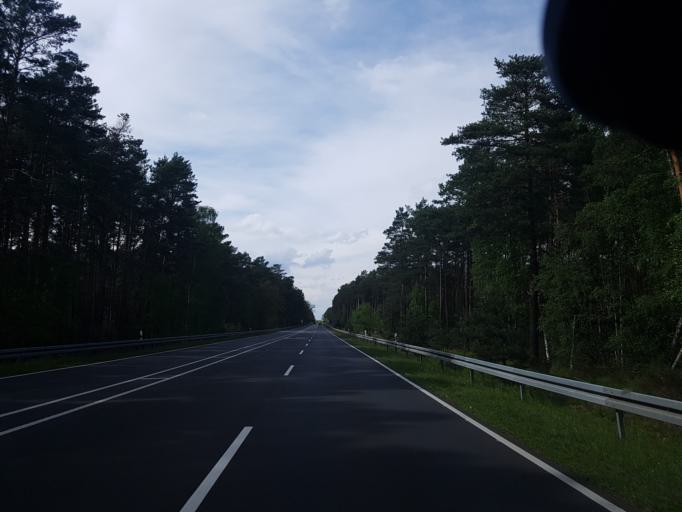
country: DE
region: Saxony
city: Gross Duben
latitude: 51.6576
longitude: 14.5315
